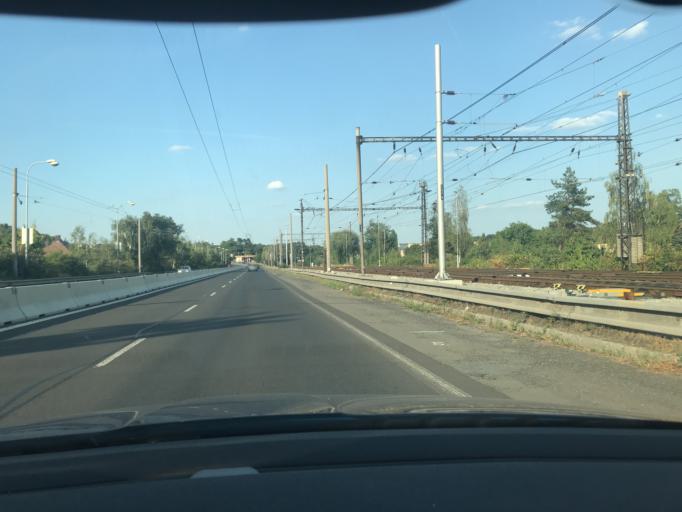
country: CZ
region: Ustecky
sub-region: Okres Chomutov
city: Chomutov
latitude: 50.4672
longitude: 13.4093
